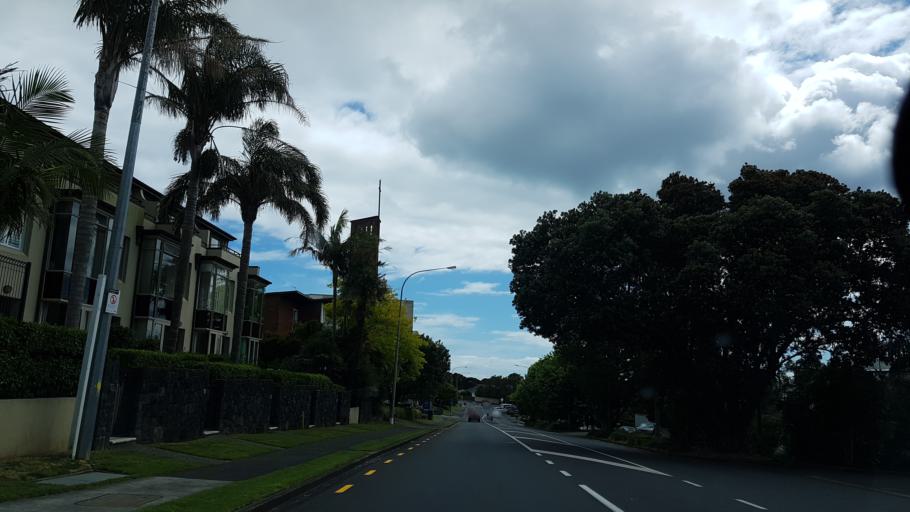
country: NZ
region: Auckland
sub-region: Auckland
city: North Shore
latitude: -36.7842
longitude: 174.7717
